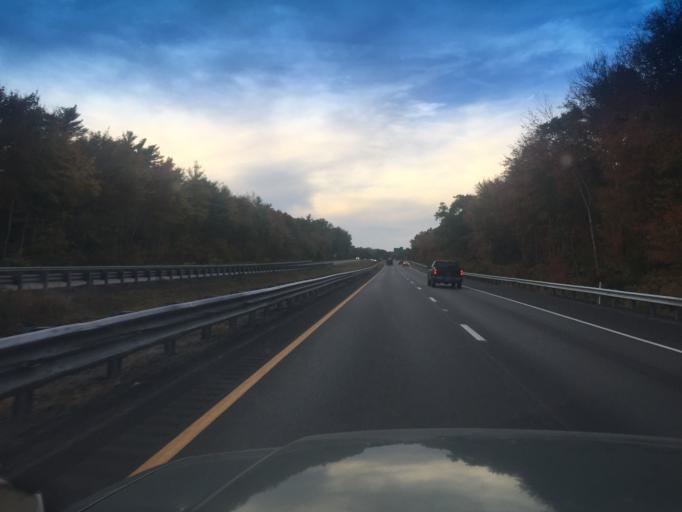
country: US
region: Massachusetts
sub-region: Plymouth County
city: Carver
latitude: 41.8446
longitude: -70.8412
